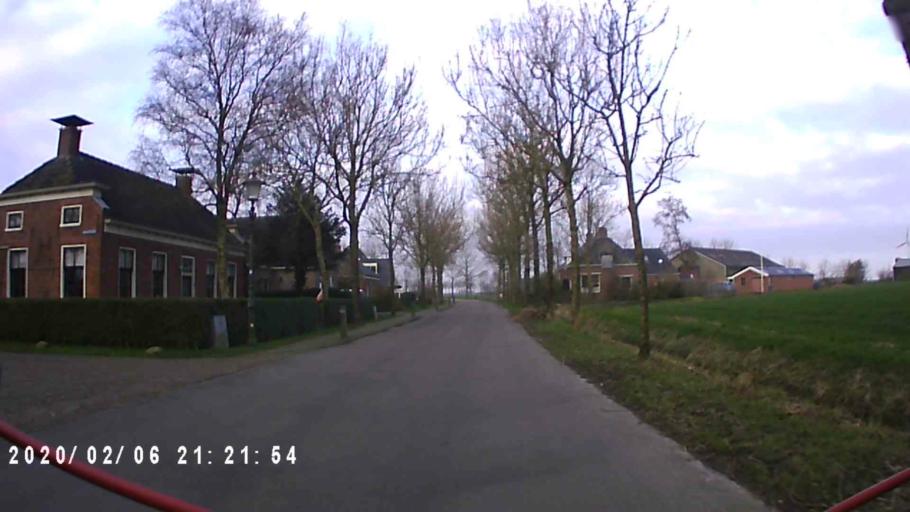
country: NL
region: Groningen
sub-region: Gemeente Zuidhorn
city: Oldehove
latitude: 53.2910
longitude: 6.3648
